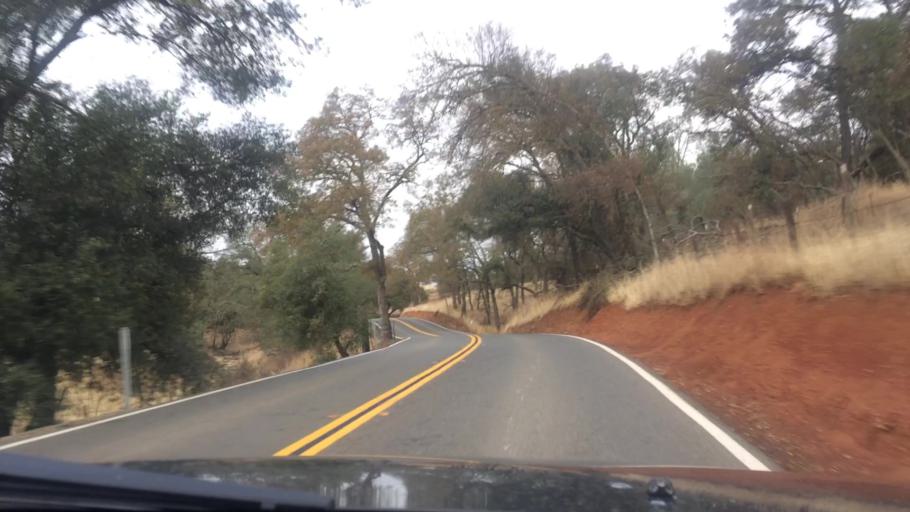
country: US
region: California
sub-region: El Dorado County
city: Cameron Park
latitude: 38.5838
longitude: -121.0056
